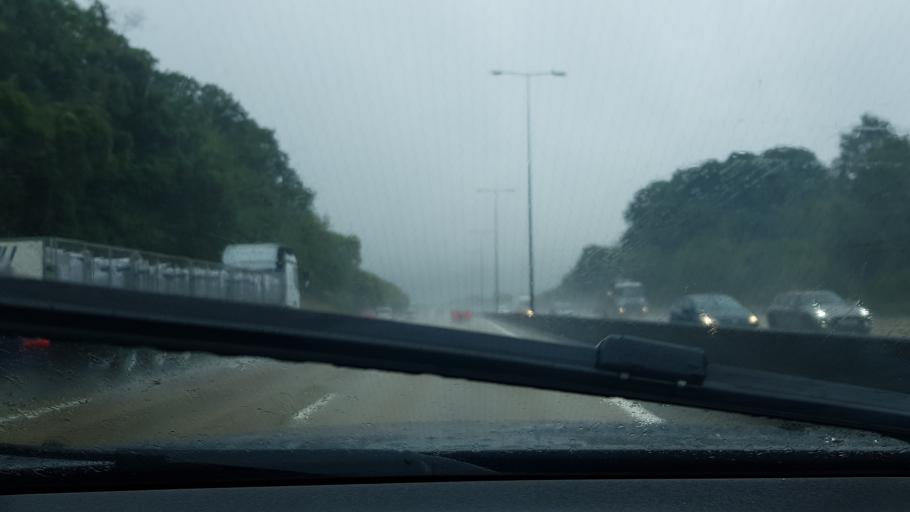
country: GB
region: England
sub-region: Surrey
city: Headley
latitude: 51.2856
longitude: -0.2699
